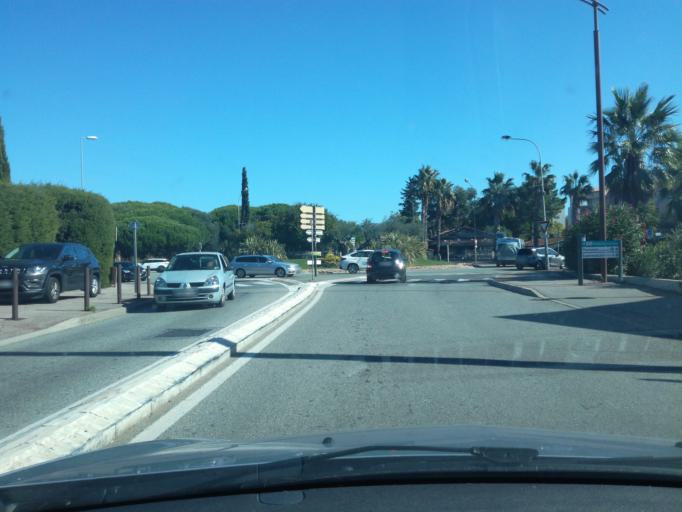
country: FR
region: Provence-Alpes-Cote d'Azur
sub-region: Departement du Var
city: Frejus
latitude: 43.4397
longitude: 6.7439
